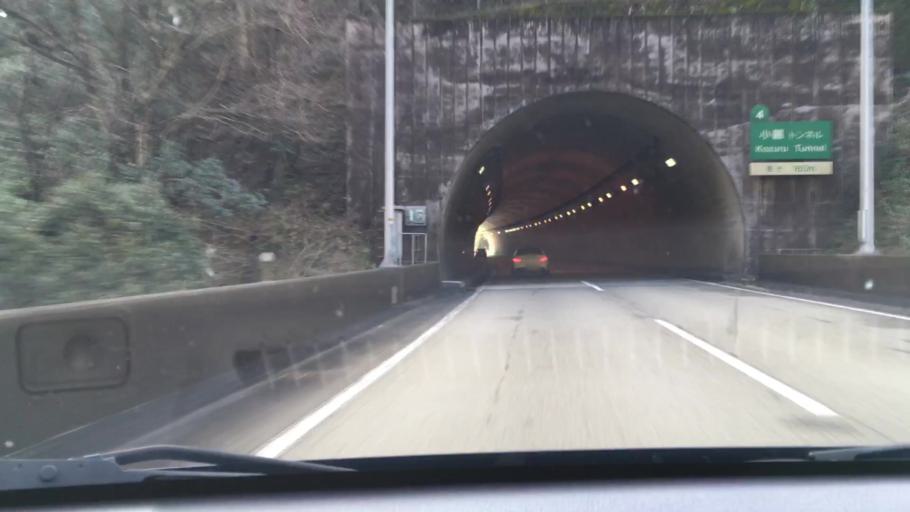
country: JP
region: Kumamoto
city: Hitoyoshi
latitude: 32.3138
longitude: 130.7487
